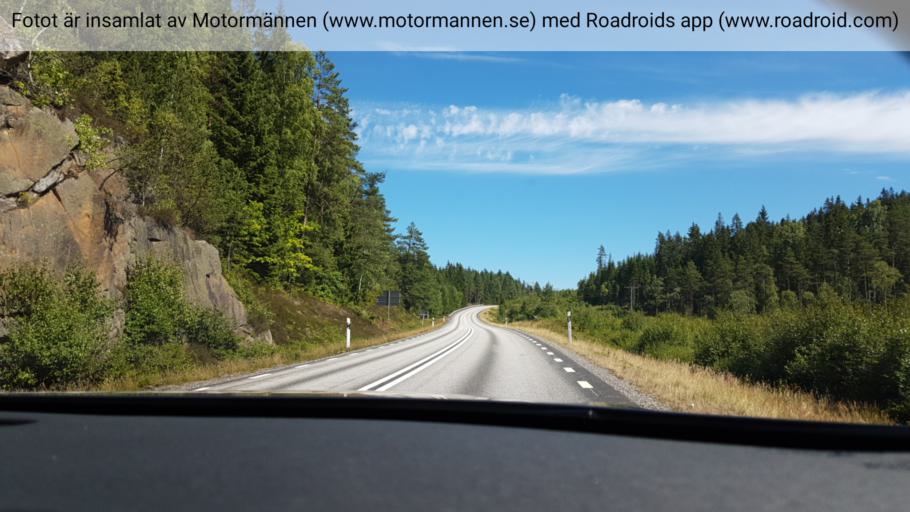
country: SE
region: Joenkoeping
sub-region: Gnosjo Kommun
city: Gnosjoe
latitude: 57.3402
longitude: 13.7769
